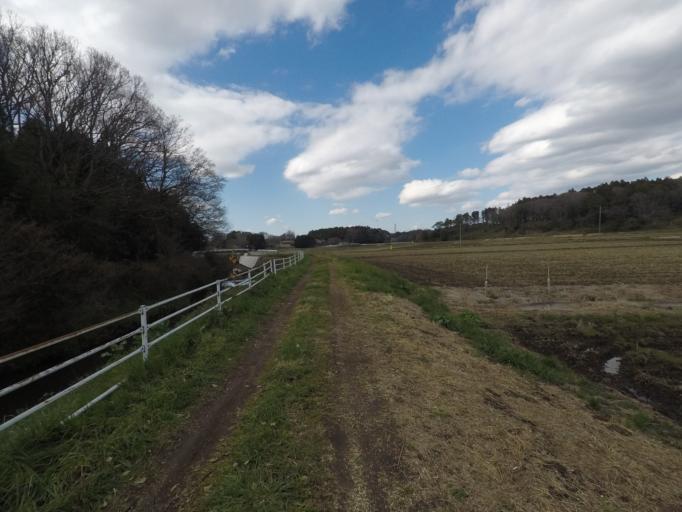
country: JP
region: Ibaraki
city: Ushiku
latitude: 35.9904
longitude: 140.1191
